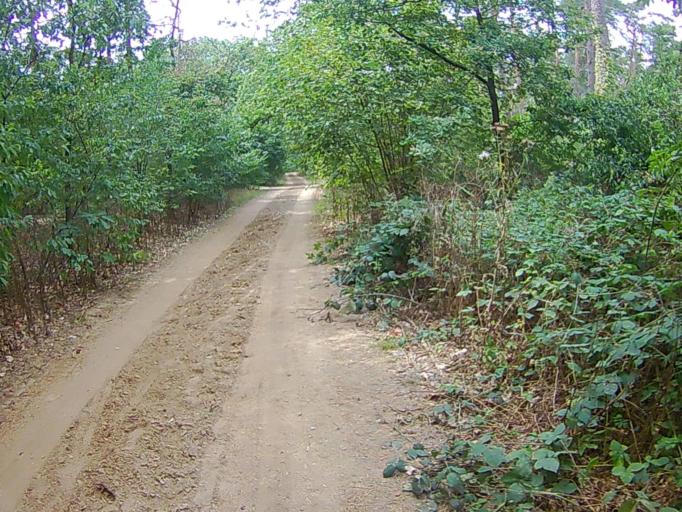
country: BE
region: Flanders
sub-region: Provincie Antwerpen
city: Kasterlee
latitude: 51.2377
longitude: 4.9520
